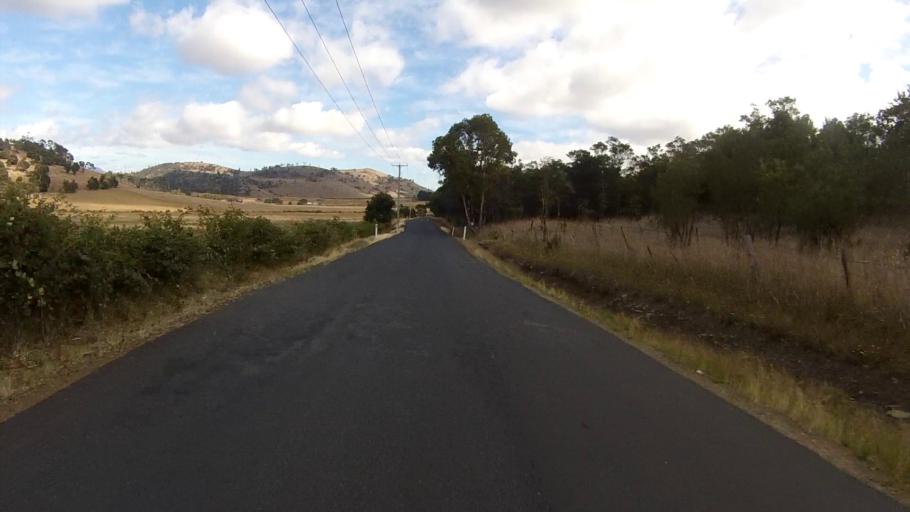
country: AU
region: Tasmania
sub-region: Brighton
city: Old Beach
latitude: -42.7515
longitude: 147.3024
